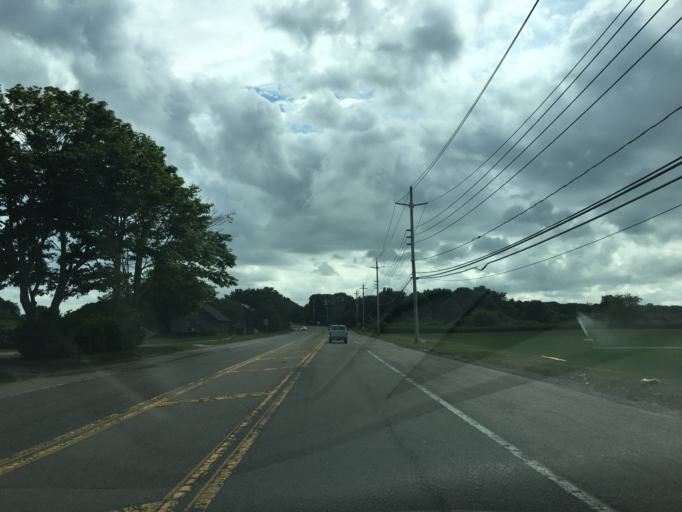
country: US
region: New York
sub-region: Suffolk County
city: Southold
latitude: 41.0680
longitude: -72.4389
